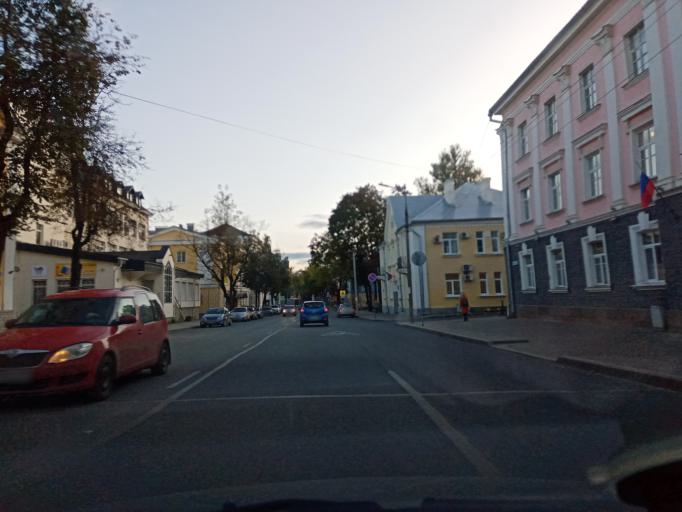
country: RU
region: Pskov
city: Pskov
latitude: 57.8137
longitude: 28.3388
